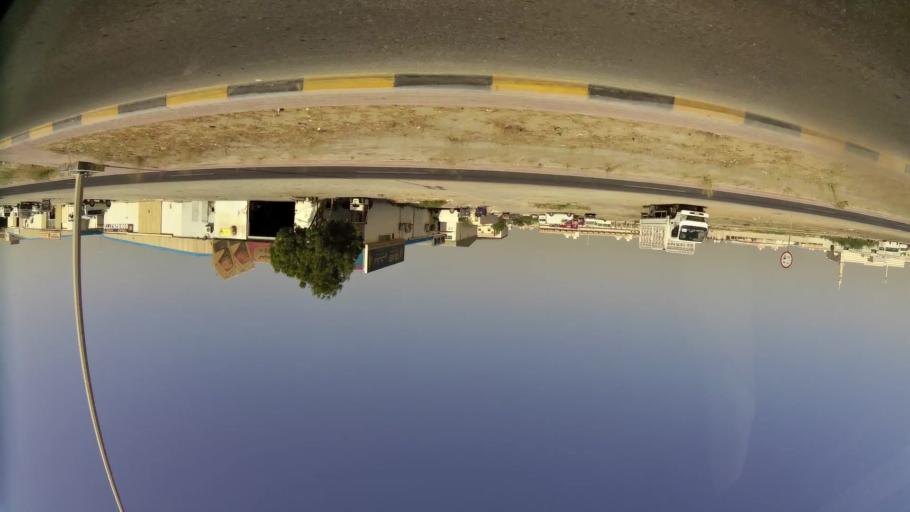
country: AE
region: Ajman
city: Ajman
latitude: 25.4373
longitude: 55.5278
